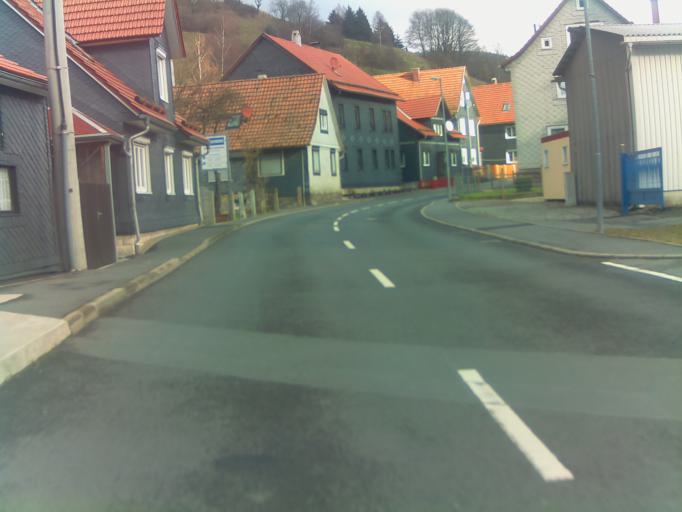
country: DE
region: Thuringia
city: Frauenwald
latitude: 50.5253
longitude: 10.8894
